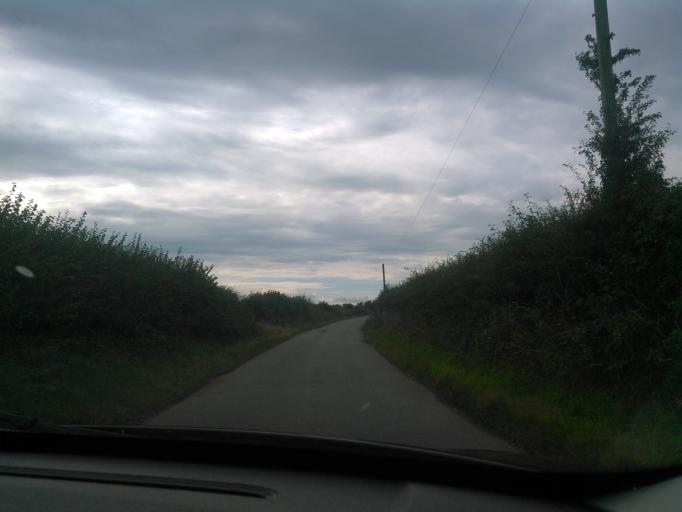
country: GB
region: England
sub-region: Shropshire
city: Stoke upon Tern
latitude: 52.8144
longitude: -2.5717
